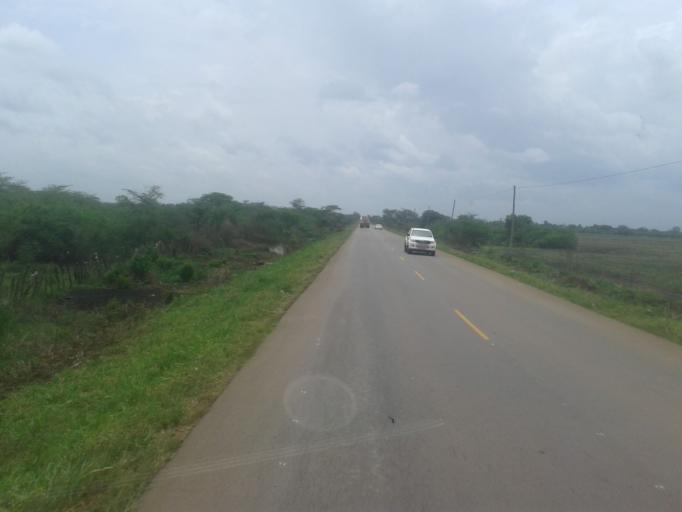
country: UG
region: Western Region
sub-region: Kiryandongo District
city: Masindi Port
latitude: 1.6271
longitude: 32.0320
